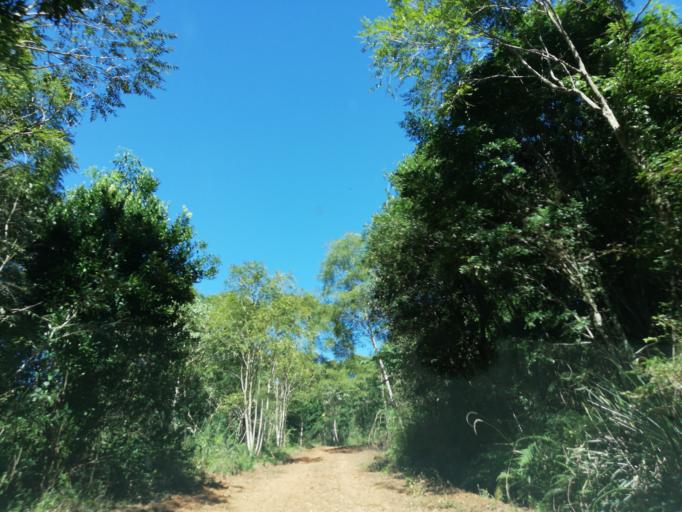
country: AR
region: Misiones
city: El Soberbio
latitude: -27.0629
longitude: -54.3743
